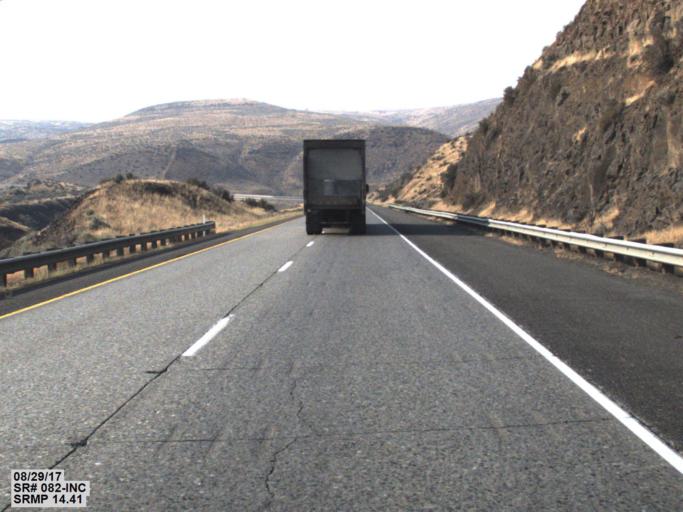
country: US
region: Washington
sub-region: Kittitas County
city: Kittitas
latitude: 46.8084
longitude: -120.3568
